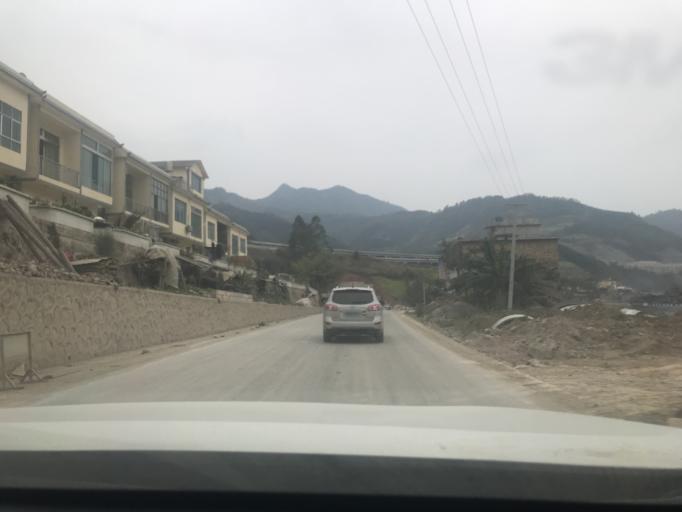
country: CN
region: Guangxi Zhuangzu Zizhiqu
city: Xinzhou
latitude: 25.0152
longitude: 105.8609
